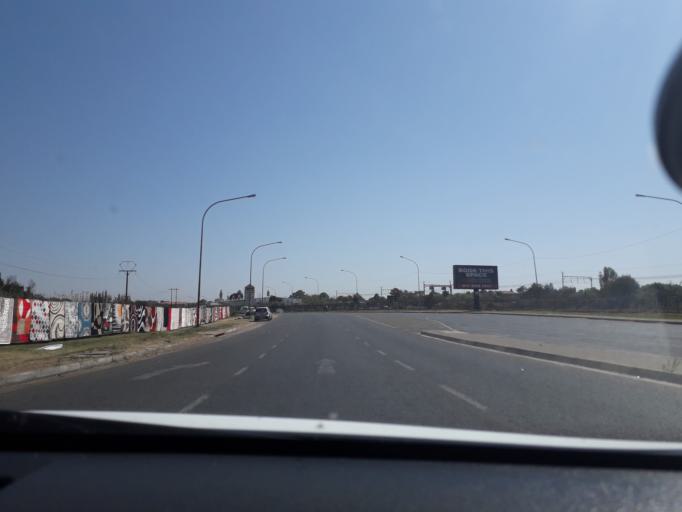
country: ZA
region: Gauteng
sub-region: City of Johannesburg Metropolitan Municipality
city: Modderfontein
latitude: -26.1007
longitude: 28.2207
